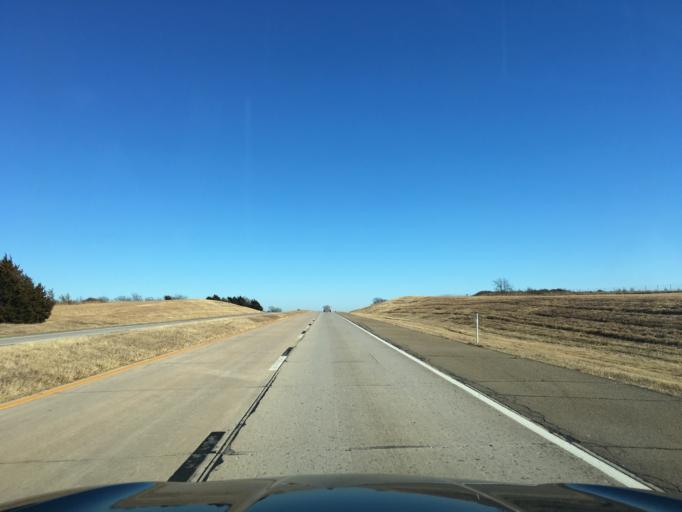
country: US
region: Oklahoma
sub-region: Payne County
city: Yale
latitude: 36.2240
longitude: -96.7353
